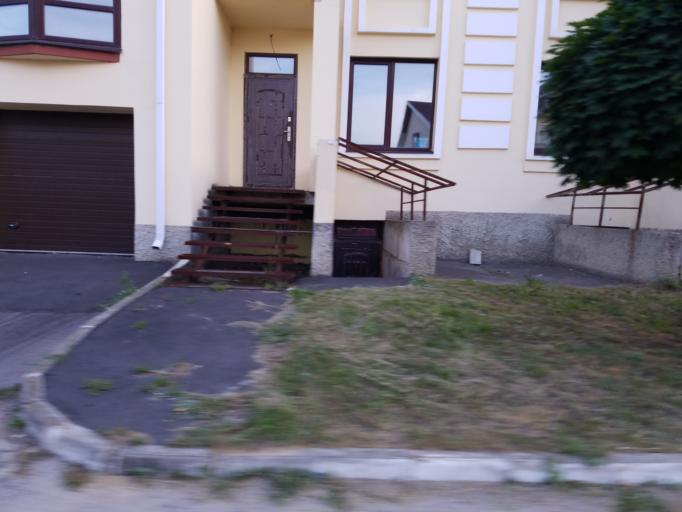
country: RU
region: Orjol
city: Znamenka
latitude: 52.9112
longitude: 36.0080
